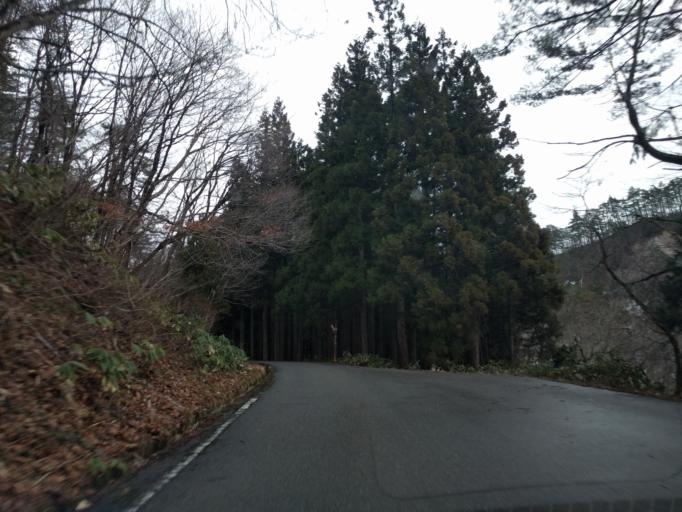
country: JP
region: Fukushima
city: Kitakata
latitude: 37.6861
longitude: 139.9328
